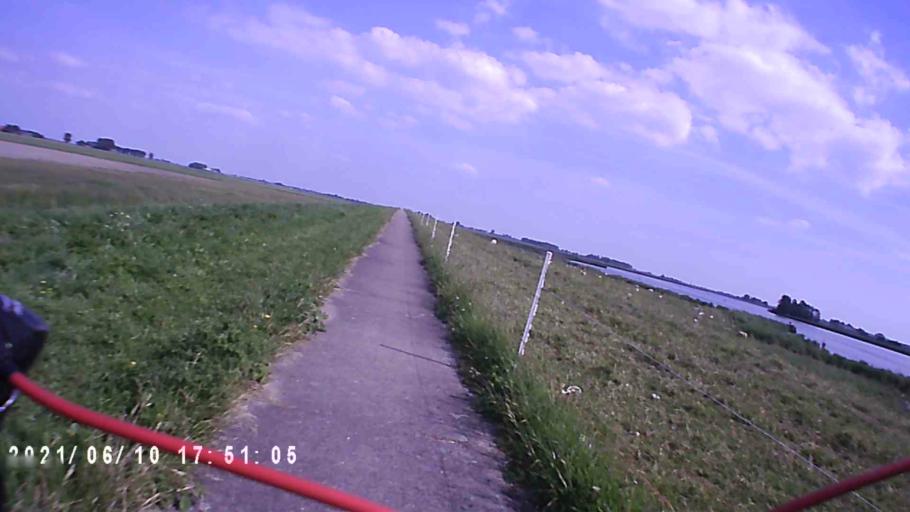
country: NL
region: Groningen
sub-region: Gemeente De Marne
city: Ulrum
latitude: 53.3312
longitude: 6.3127
